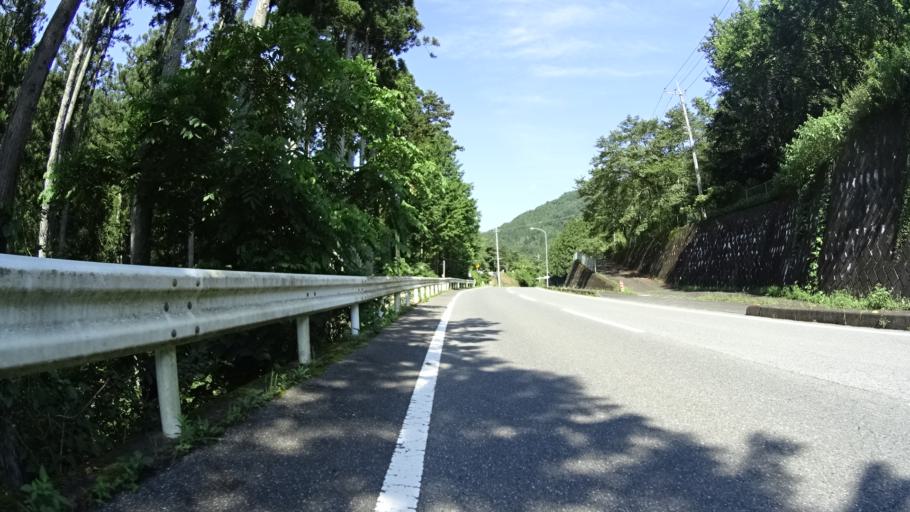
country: JP
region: Saitama
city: Chichibu
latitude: 36.0356
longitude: 138.9190
